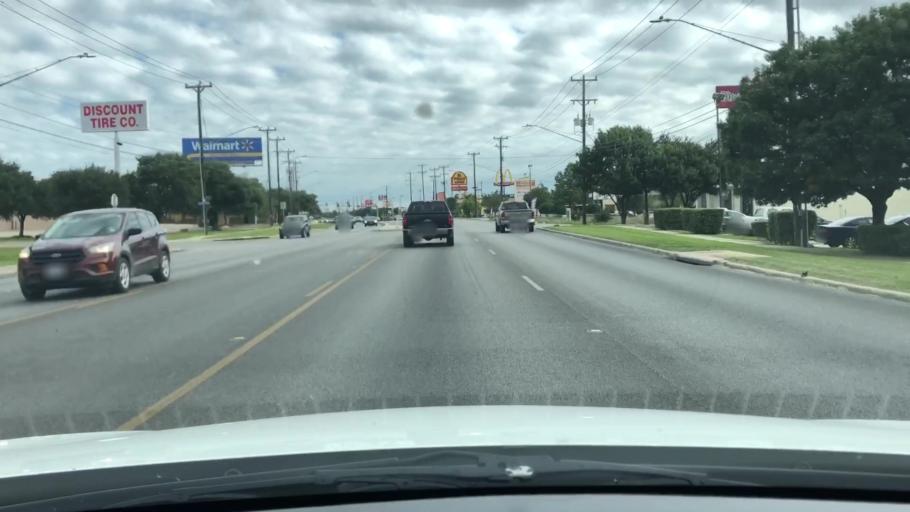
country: US
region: Texas
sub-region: Bexar County
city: Leon Valley
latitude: 29.4859
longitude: -98.6691
